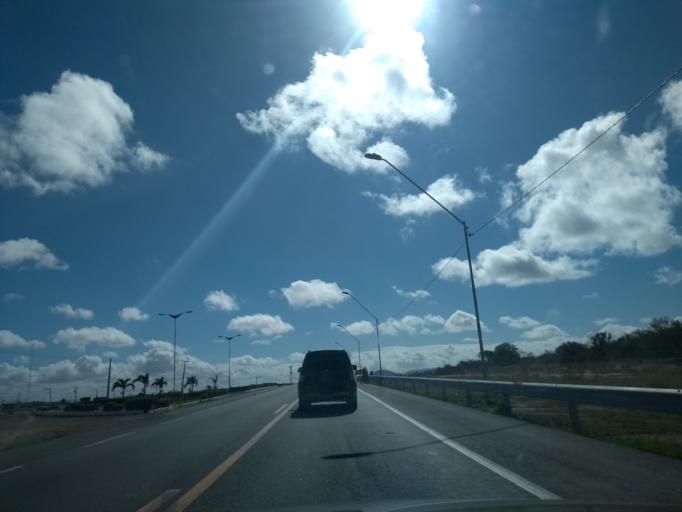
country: BR
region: Bahia
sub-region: Amargosa
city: Amargosa
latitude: -12.8610
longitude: -39.8513
